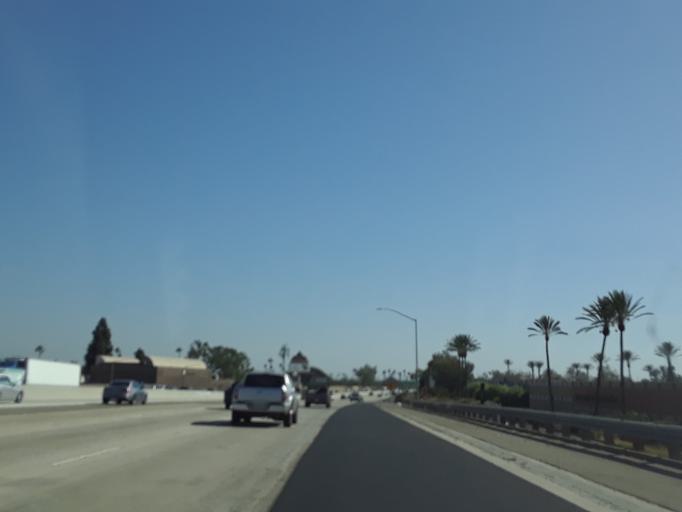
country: US
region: California
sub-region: Los Angeles County
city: Hawaiian Gardens
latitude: 33.8310
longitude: -118.0842
